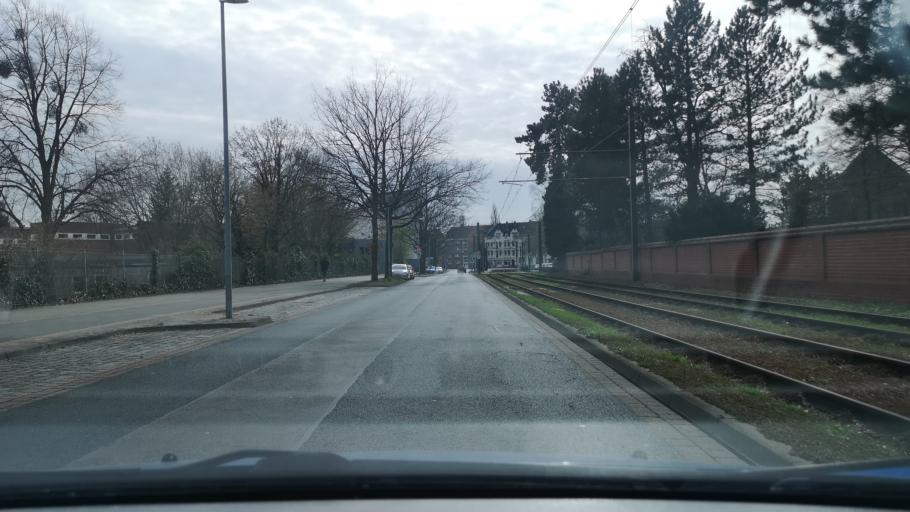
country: DE
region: Lower Saxony
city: Hannover
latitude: 52.4021
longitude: 9.6708
